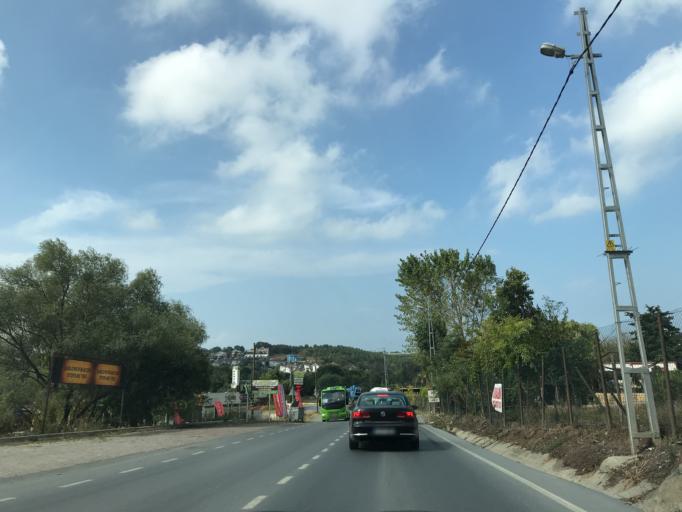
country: TR
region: Istanbul
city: Arikoey
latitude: 41.2178
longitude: 29.0350
